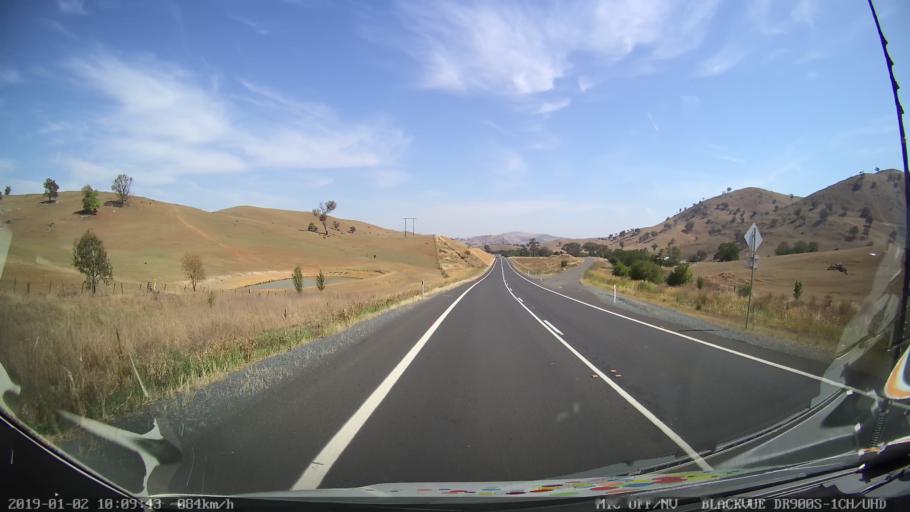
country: AU
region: New South Wales
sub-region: Gundagai
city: Gundagai
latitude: -35.1135
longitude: 148.0977
